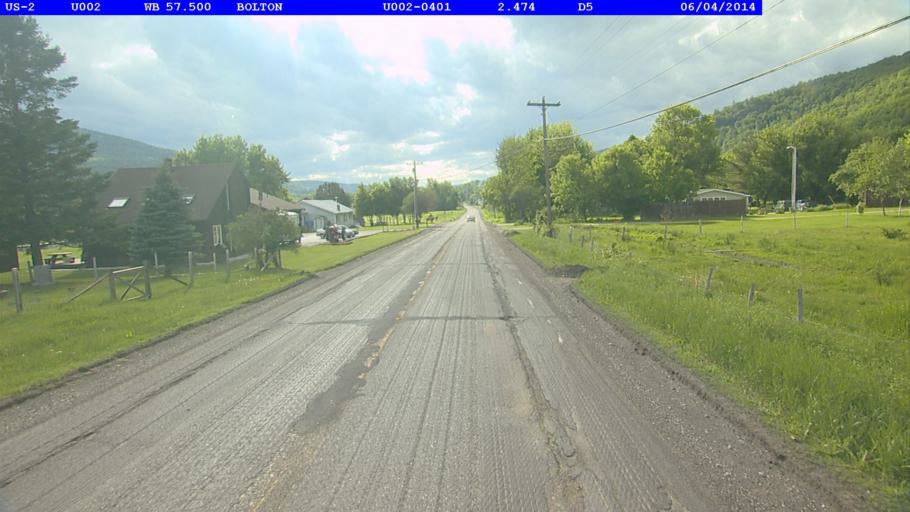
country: US
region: Vermont
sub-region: Washington County
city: Waterbury
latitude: 44.3738
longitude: -72.8857
